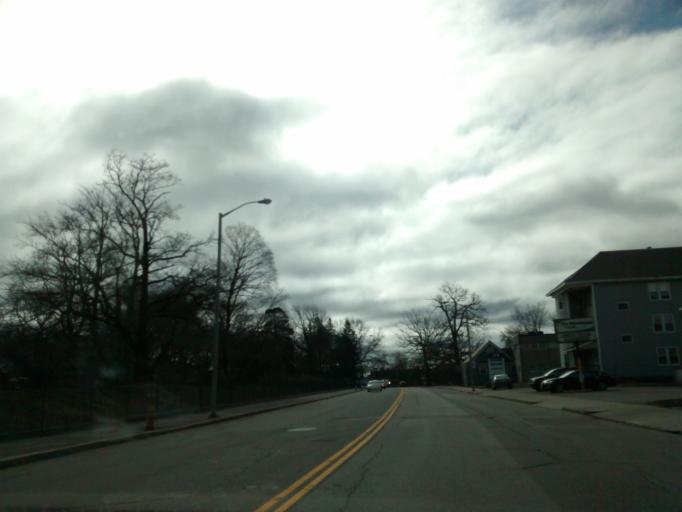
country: US
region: Massachusetts
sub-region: Worcester County
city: Worcester
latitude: 42.2802
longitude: -71.8051
